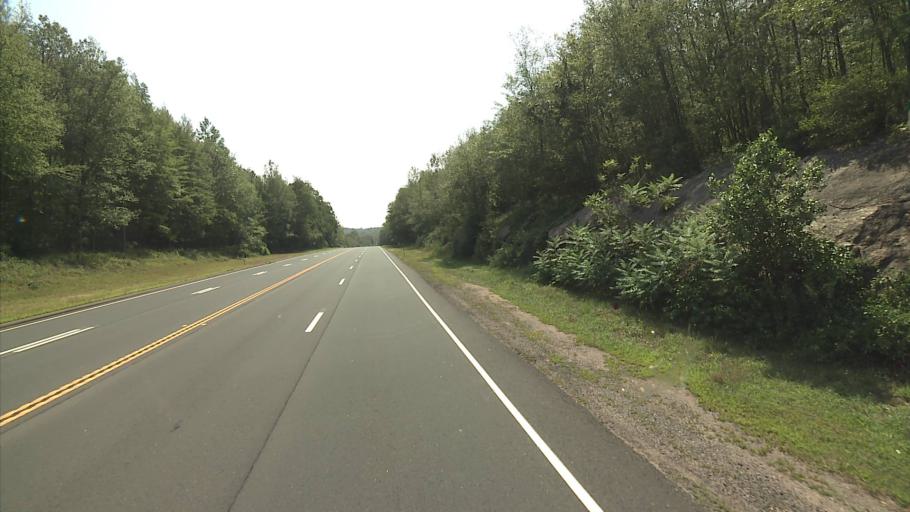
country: US
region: Connecticut
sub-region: Middlesex County
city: East Haddam
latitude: 41.4284
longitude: -72.4905
